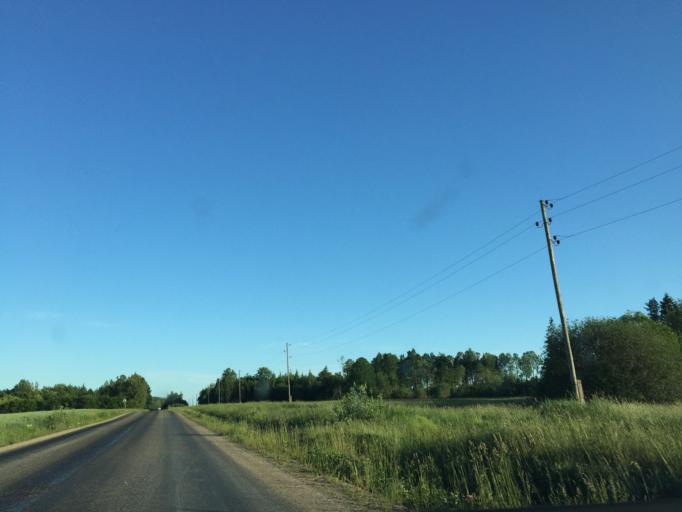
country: LV
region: Broceni
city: Broceni
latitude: 56.7158
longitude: 22.5013
